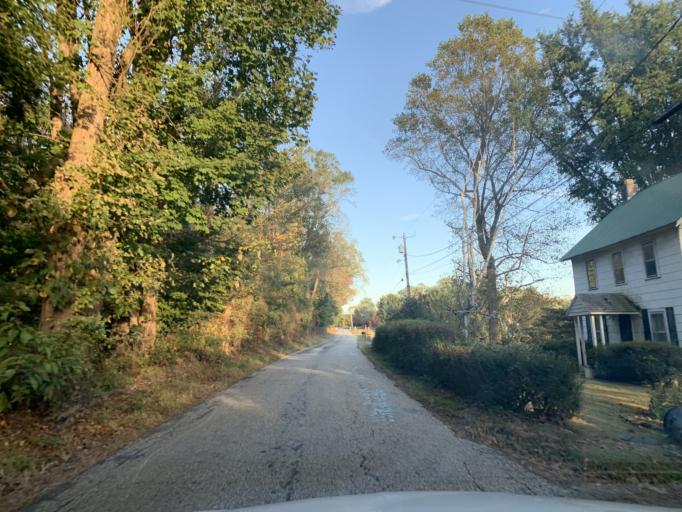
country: US
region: Maryland
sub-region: Harford County
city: Fallston
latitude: 39.4991
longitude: -76.4414
